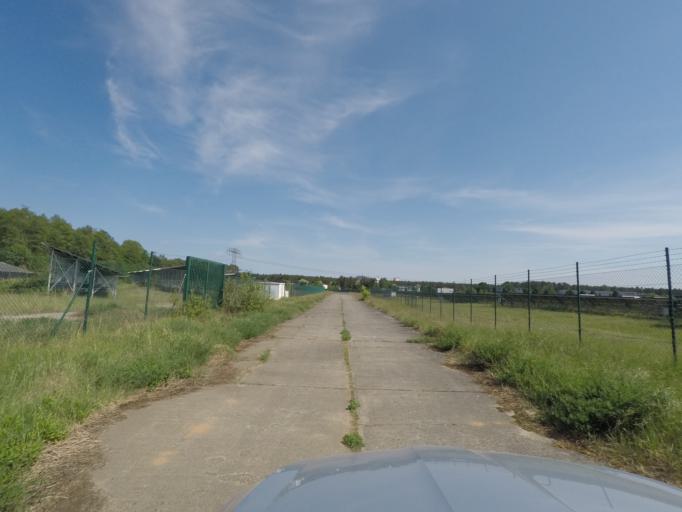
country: DE
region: Brandenburg
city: Britz
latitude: 52.8590
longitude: 13.7696
